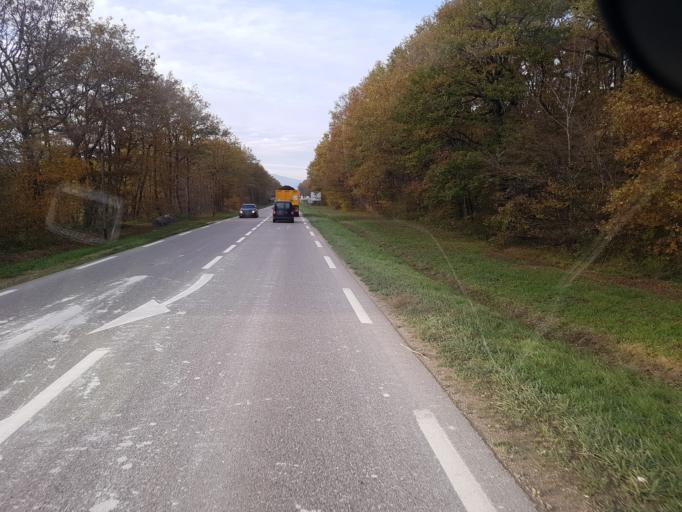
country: FR
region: Rhone-Alpes
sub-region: Departement de l'Ain
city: Bellegarde-sur-Valserine
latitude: 46.0586
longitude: 5.8683
